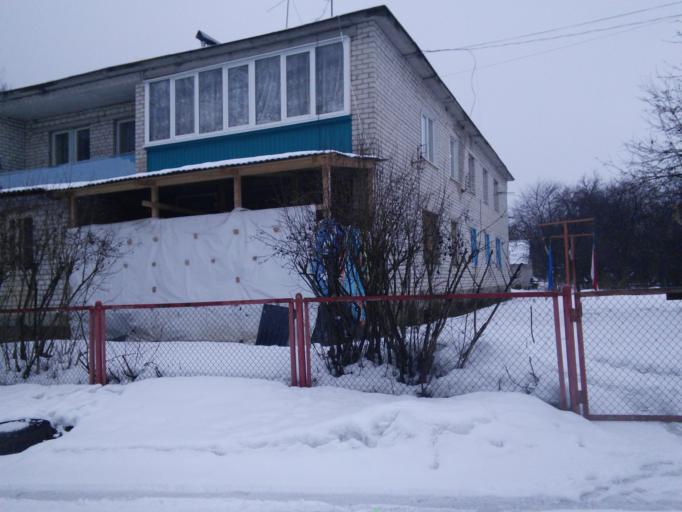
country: RU
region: Kursk
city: Chernitsyno
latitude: 51.5695
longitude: 36.0855
